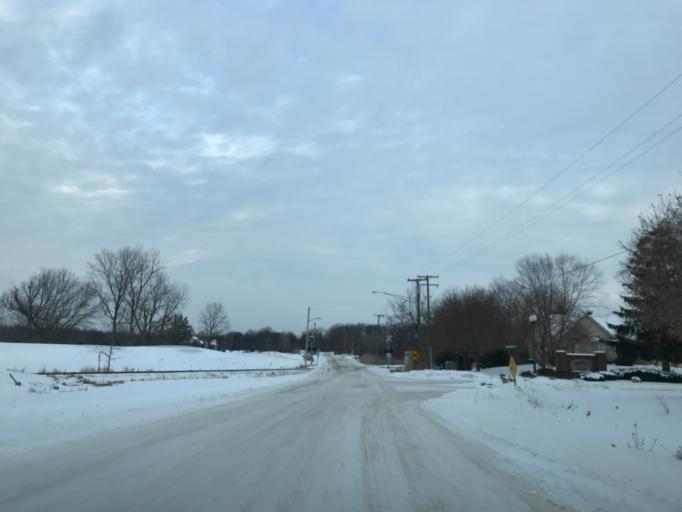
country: US
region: Michigan
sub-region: Livingston County
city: Whitmore Lake
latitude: 42.4014
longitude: -83.7443
